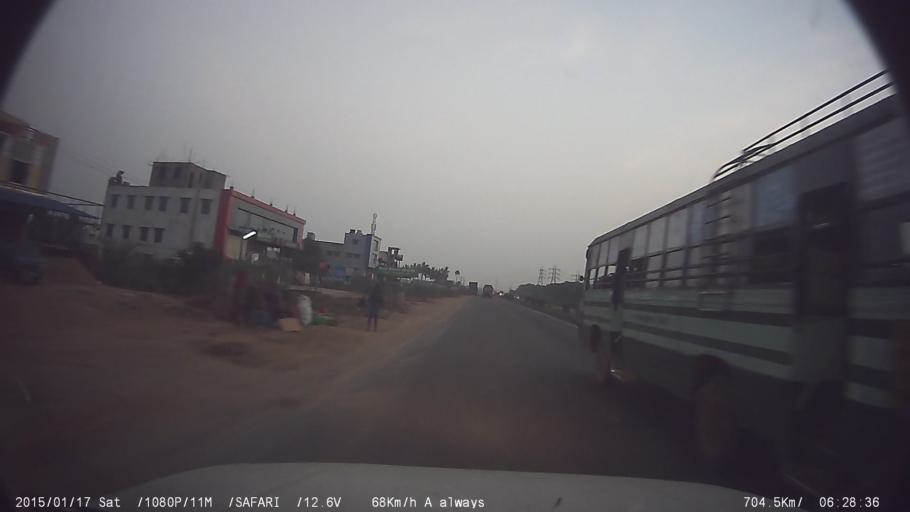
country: IN
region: Tamil Nadu
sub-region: Kancheepuram
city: Sriperumbudur
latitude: 12.9356
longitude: 79.9107
